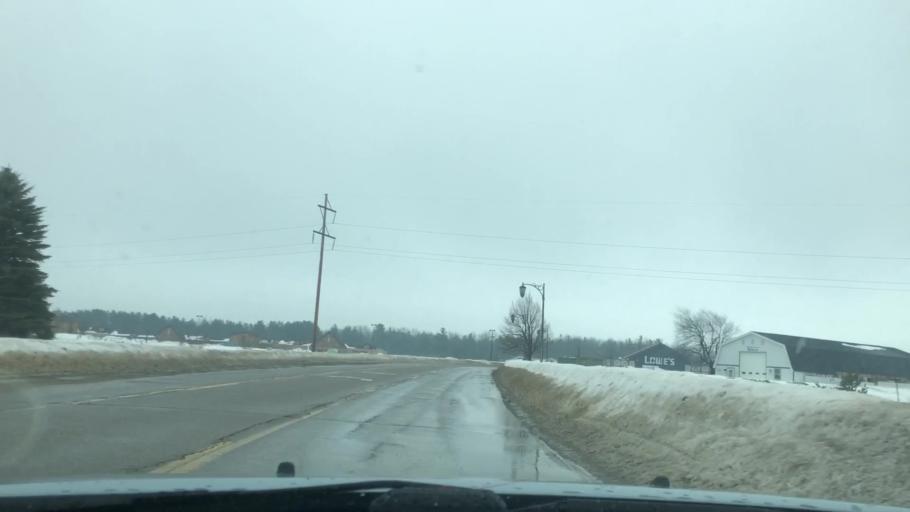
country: US
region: Michigan
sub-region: Otsego County
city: Gaylord
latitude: 45.0261
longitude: -84.6942
